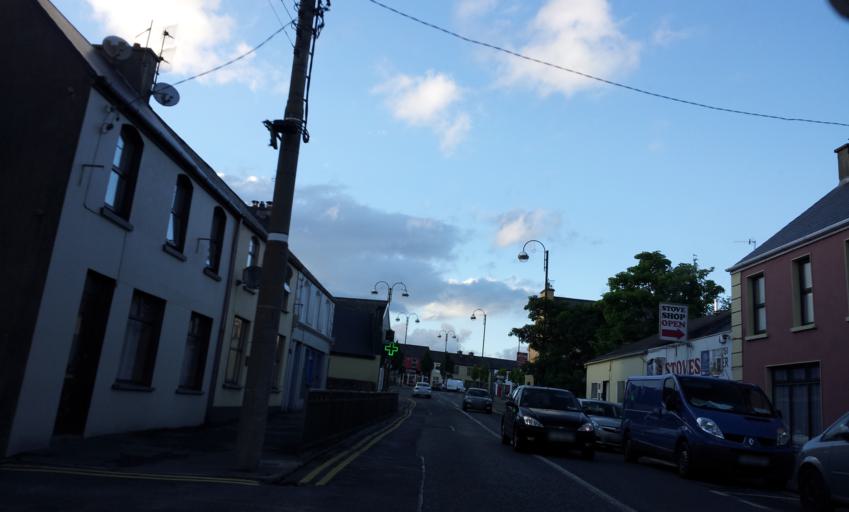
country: IE
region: Munster
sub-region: County Limerick
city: Abbeyfeale
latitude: 52.3835
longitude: -9.3017
